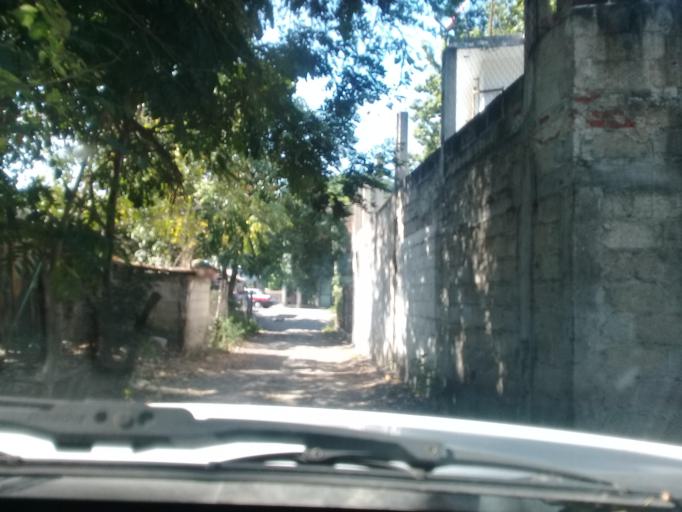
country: MX
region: Veracruz
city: Actopan
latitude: 19.4727
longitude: -96.5775
